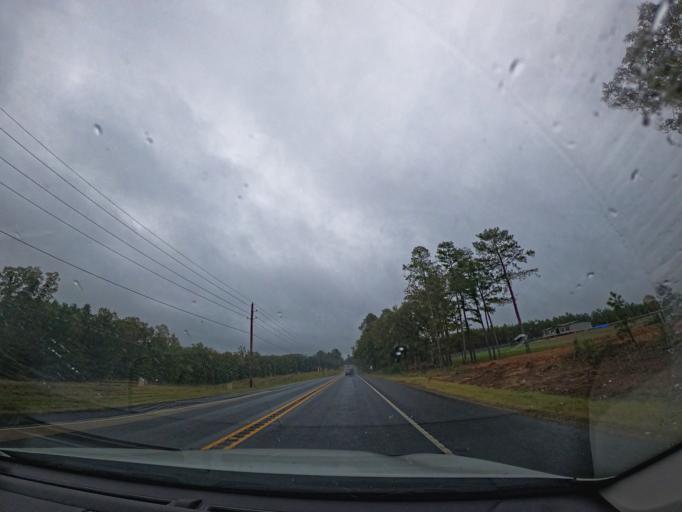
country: US
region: Louisiana
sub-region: Caddo Parish
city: Greenwood
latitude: 32.3983
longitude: -94.0030
